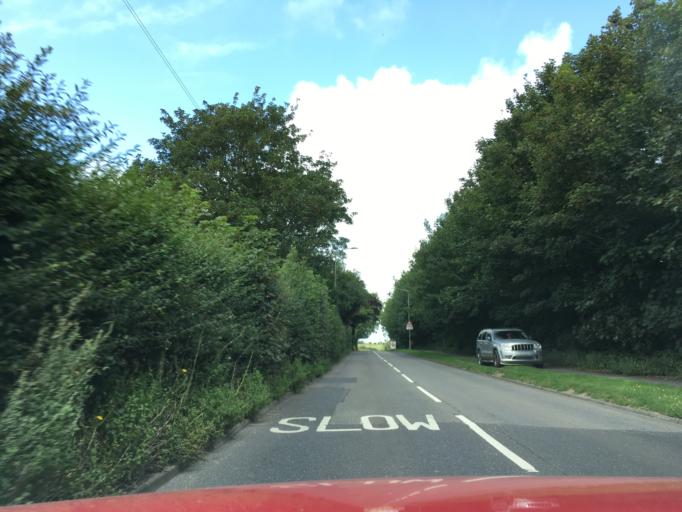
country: GB
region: England
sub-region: Brighton and Hove
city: Rottingdean
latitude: 50.8258
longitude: -0.0695
